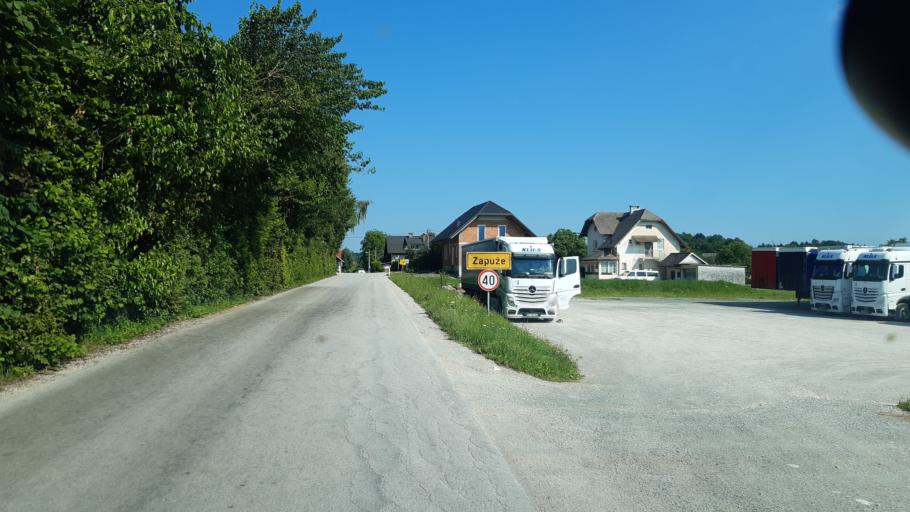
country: SI
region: Radovljica
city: Radovljica
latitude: 46.3660
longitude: 14.1904
